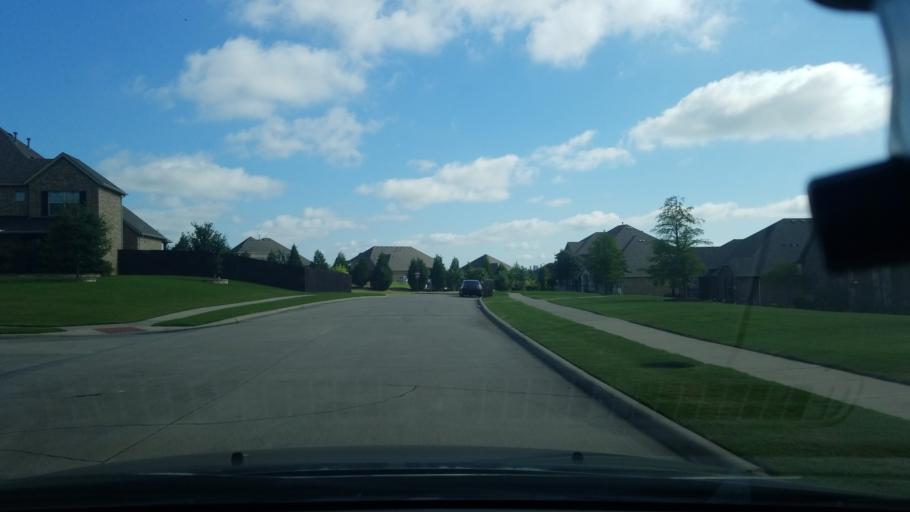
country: US
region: Texas
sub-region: Dallas County
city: Sunnyvale
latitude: 32.8050
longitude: -96.5667
